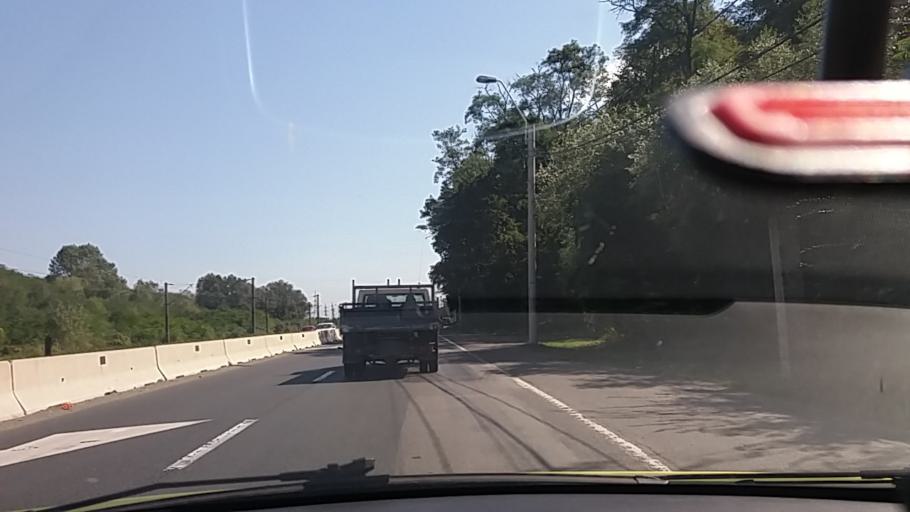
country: RO
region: Hunedoara
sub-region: Comuna Soimus
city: Soimus
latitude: 45.9033
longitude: 22.8826
